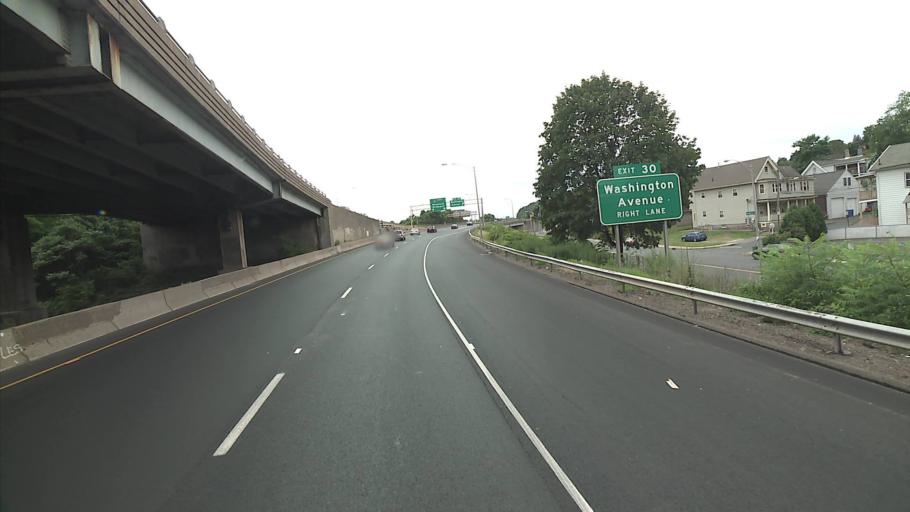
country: US
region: Connecticut
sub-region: New Haven County
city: Waterbury
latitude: 41.5474
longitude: -73.0450
